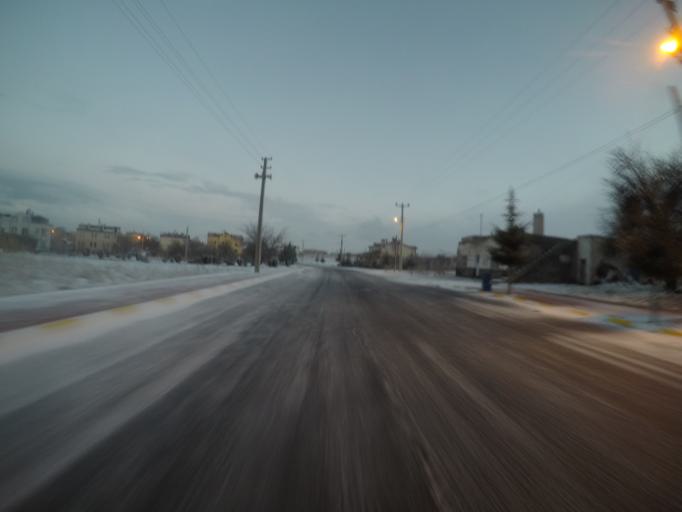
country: TR
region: Nevsehir
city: Goereme
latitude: 38.6228
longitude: 34.7992
